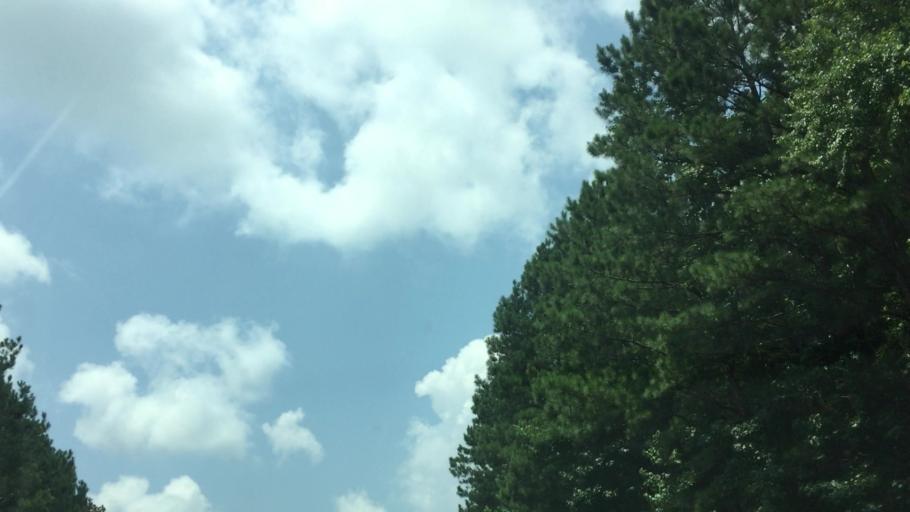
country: US
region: Georgia
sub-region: Fulton County
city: Chattahoochee Hills
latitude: 33.5637
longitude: -84.7530
